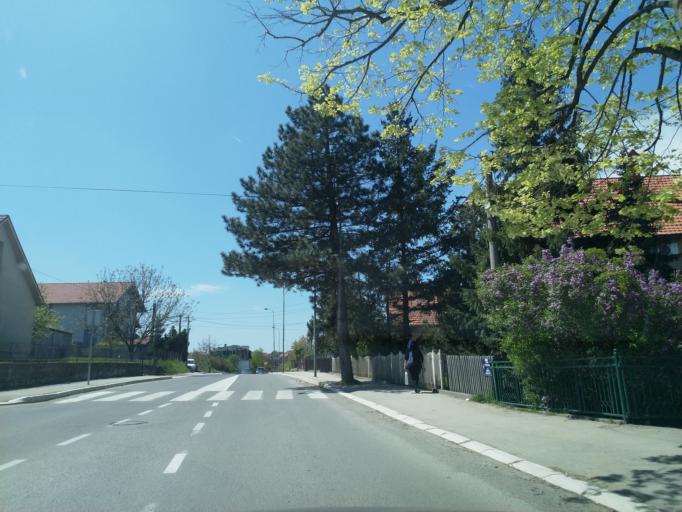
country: RS
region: Central Serbia
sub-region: Belgrade
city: Lazarevac
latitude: 44.3773
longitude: 20.2559
